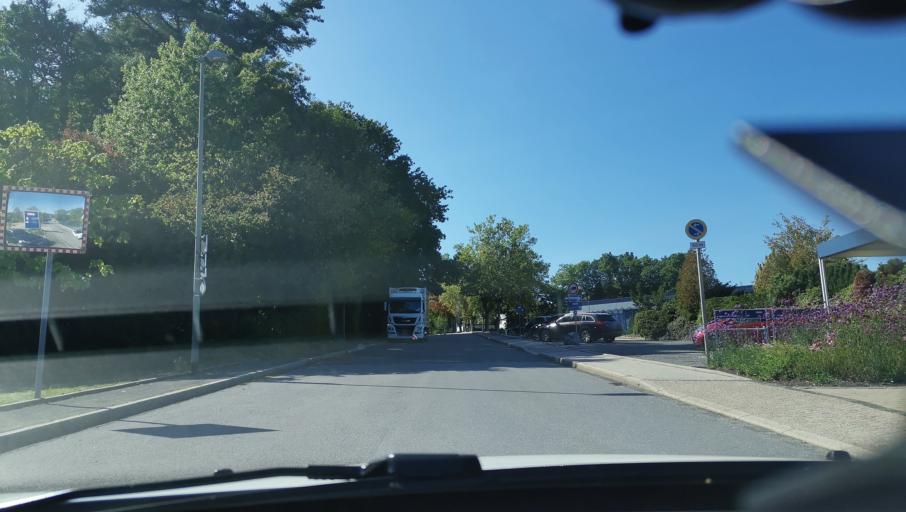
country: DE
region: North Rhine-Westphalia
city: Wetter (Ruhr)
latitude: 51.3565
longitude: 7.3836
